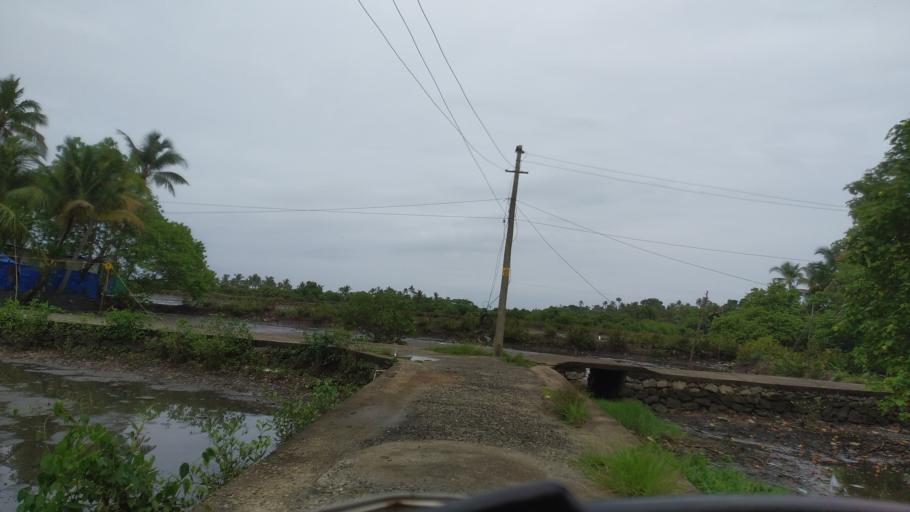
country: IN
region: Kerala
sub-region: Ernakulam
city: Elur
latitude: 10.0808
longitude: 76.2217
